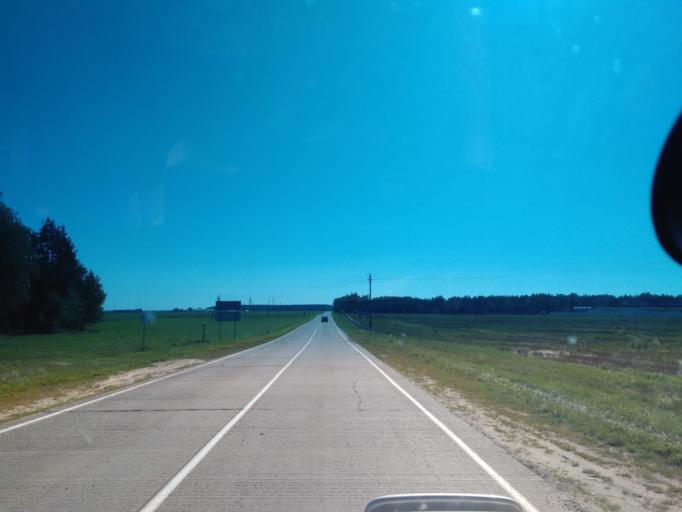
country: BY
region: Minsk
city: Stan'kava
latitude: 53.6267
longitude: 27.2584
